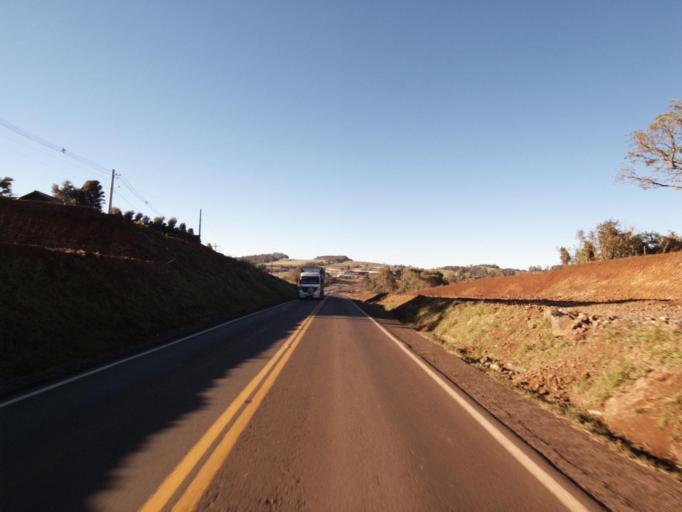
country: AR
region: Misiones
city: Bernardo de Irigoyen
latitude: -26.4250
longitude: -53.5230
